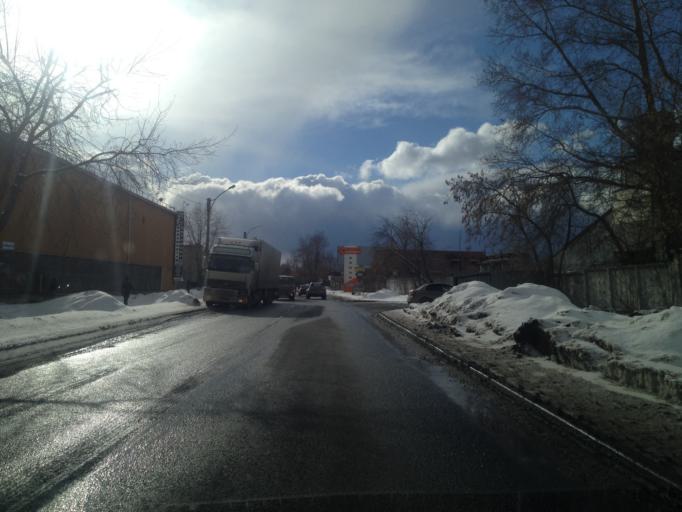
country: RU
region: Sverdlovsk
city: Yekaterinburg
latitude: 56.8699
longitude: 60.5970
